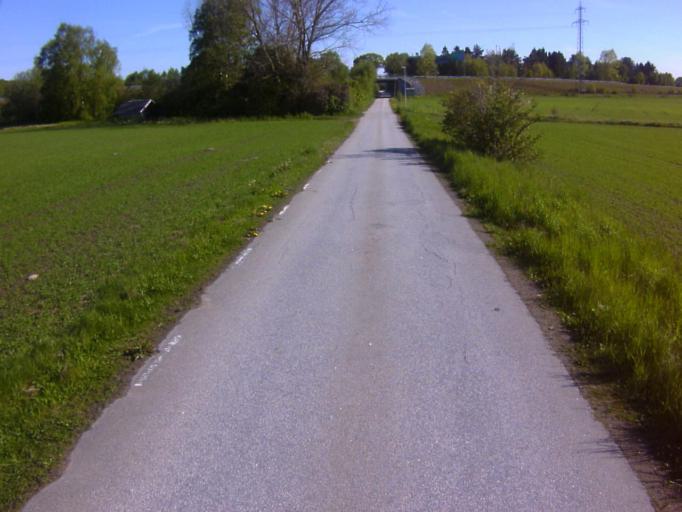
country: SE
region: Blekinge
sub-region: Solvesborgs Kommun
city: Soelvesborg
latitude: 56.0636
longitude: 14.6085
